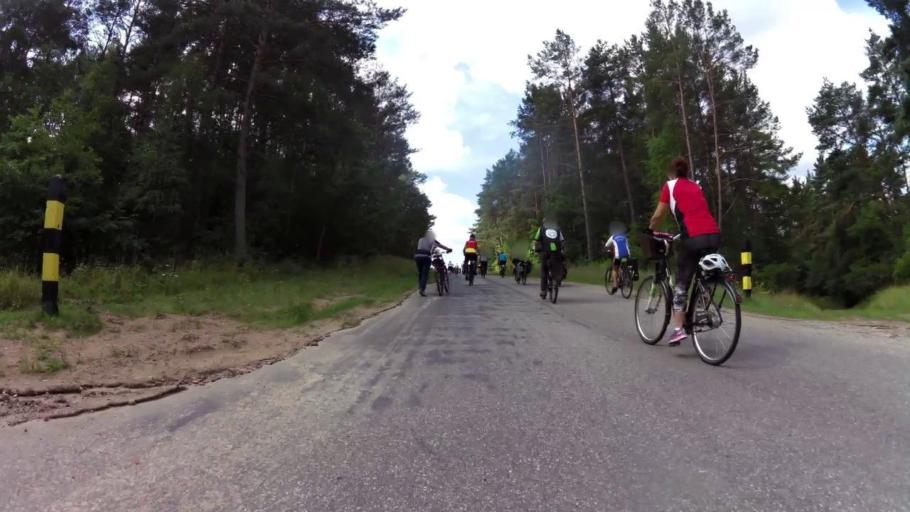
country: PL
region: West Pomeranian Voivodeship
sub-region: Powiat drawski
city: Drawsko Pomorskie
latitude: 53.4583
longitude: 15.7781
